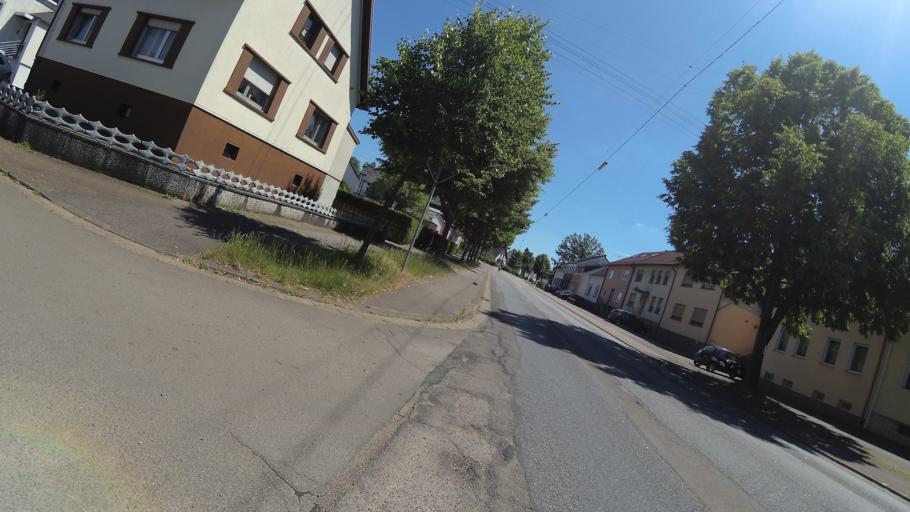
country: DE
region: Saarland
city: Saarwellingen
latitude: 49.3614
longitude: 6.8004
